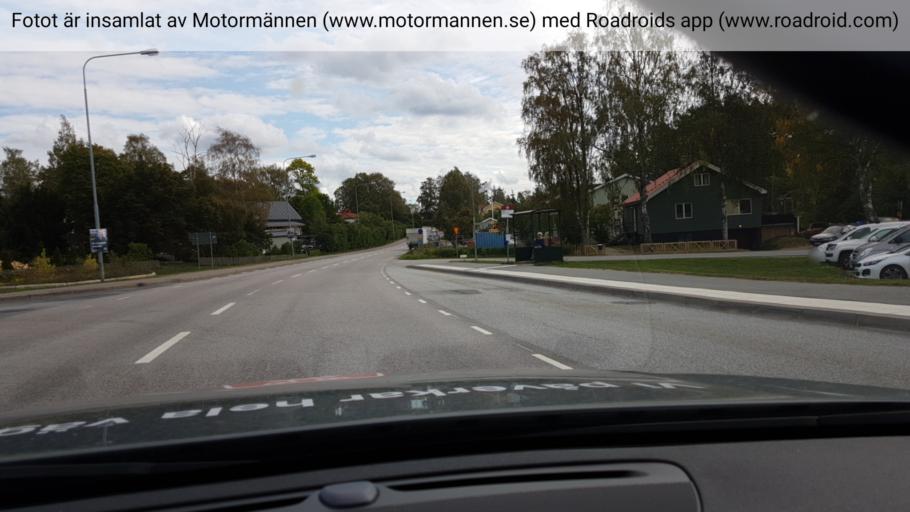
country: SE
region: Stockholm
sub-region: Norrtalje Kommun
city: Rimbo
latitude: 59.7430
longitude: 18.3567
